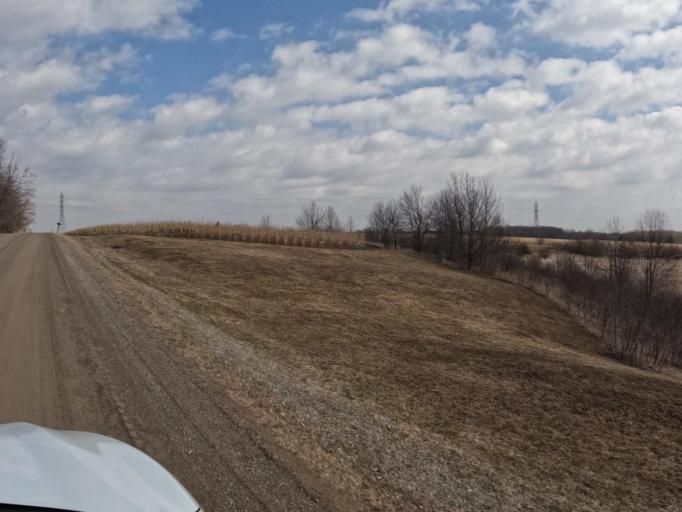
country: CA
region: Ontario
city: Orangeville
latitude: 43.9378
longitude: -80.2432
